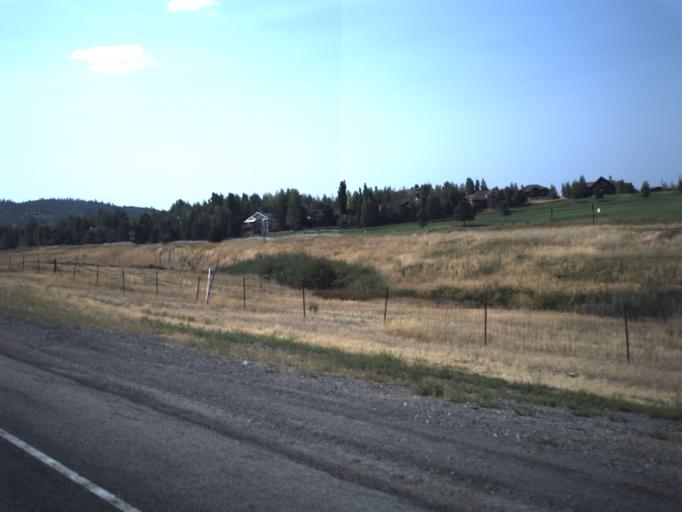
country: US
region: Utah
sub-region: Summit County
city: Summit Park
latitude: 40.7549
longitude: -111.5733
